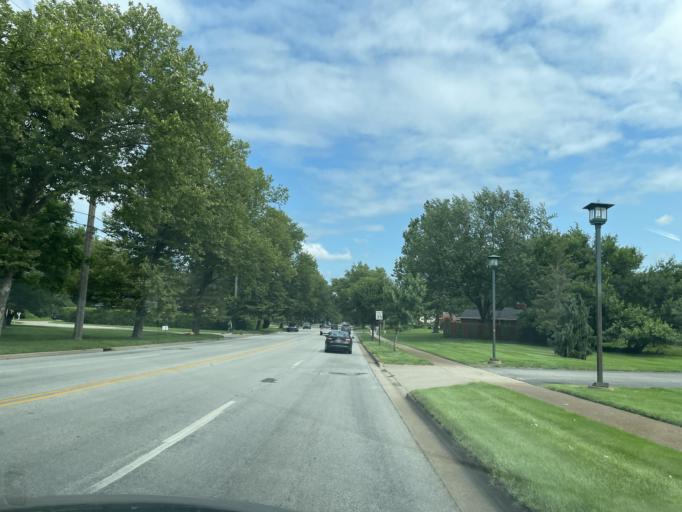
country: US
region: Michigan
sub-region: Kent County
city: Kentwood
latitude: 42.8988
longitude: -85.6267
